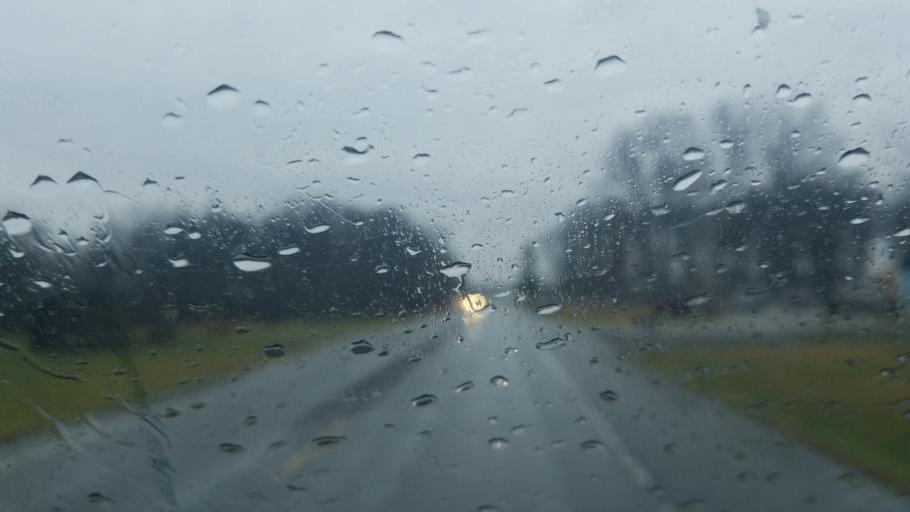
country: US
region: Indiana
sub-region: Bartholomew County
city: Columbus
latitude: 39.1923
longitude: -85.8542
